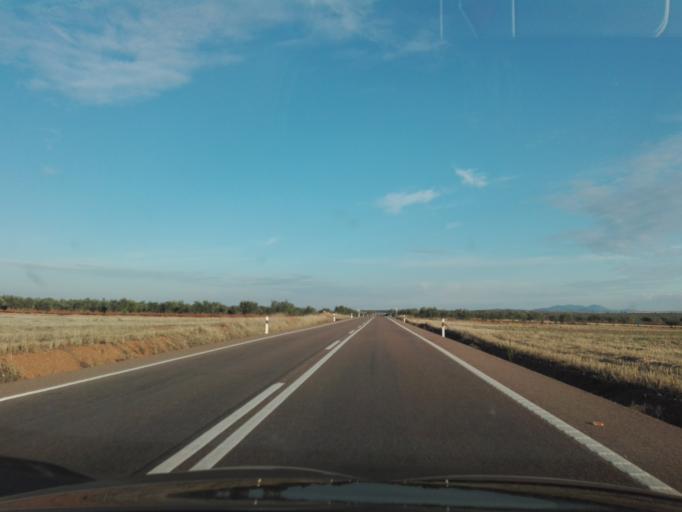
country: ES
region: Extremadura
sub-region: Provincia de Badajoz
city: Usagre
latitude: 38.3541
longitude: -6.2021
